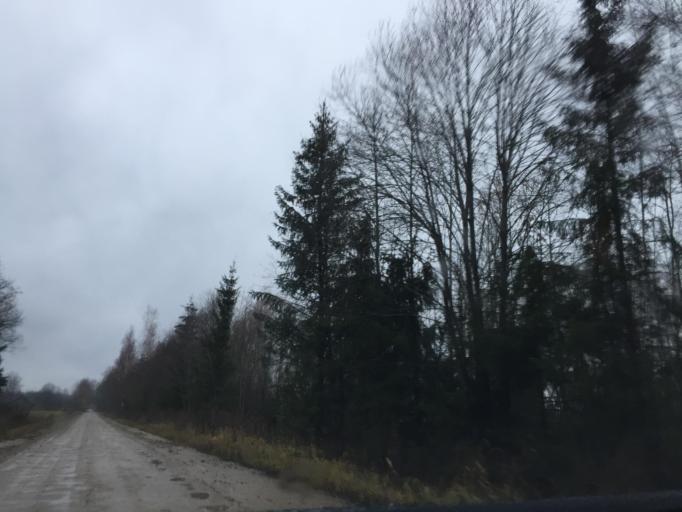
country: LV
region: Aloja
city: Staicele
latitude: 57.7524
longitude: 24.6009
